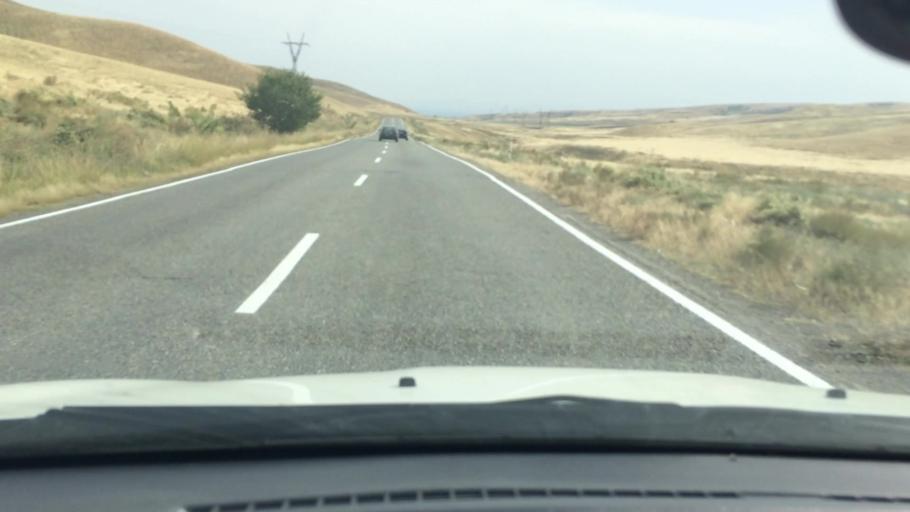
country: GE
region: Kvemo Kartli
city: Rust'avi
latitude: 41.5105
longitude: 44.9484
